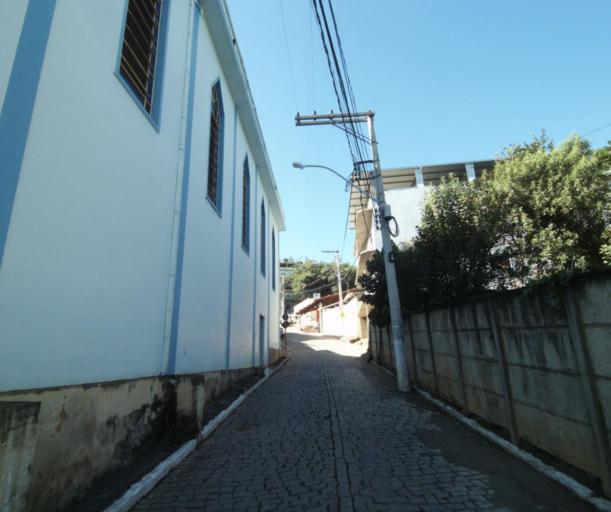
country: BR
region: Minas Gerais
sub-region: Espera Feliz
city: Espera Feliz
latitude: -20.6909
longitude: -41.8471
